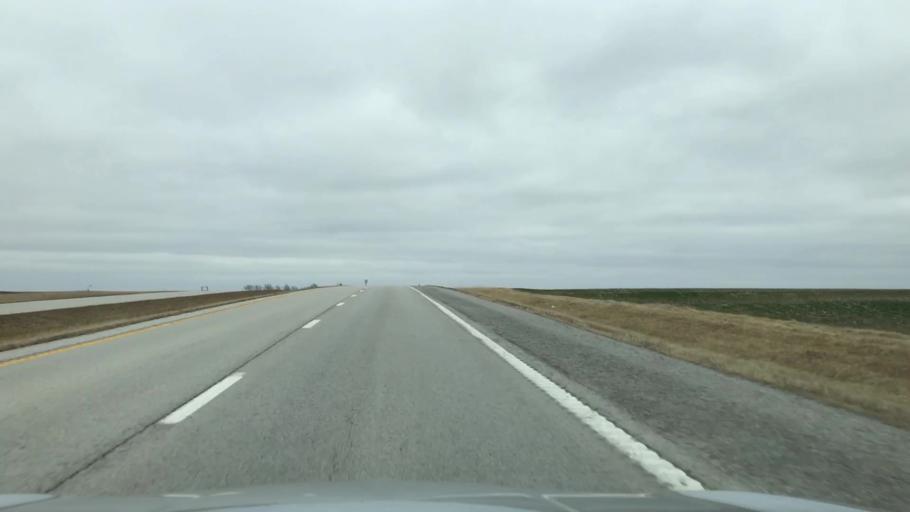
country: US
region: Missouri
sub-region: Livingston County
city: Chillicothe
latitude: 39.7761
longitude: -93.4804
